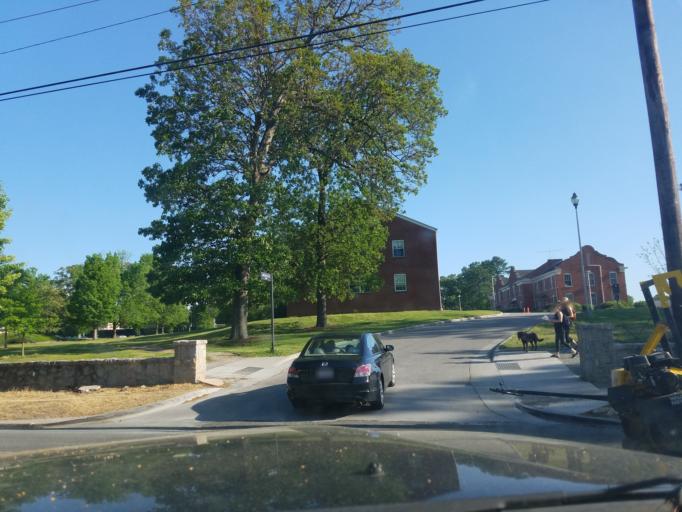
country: US
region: North Carolina
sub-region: Durham County
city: Durham
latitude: 36.0099
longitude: -78.9172
